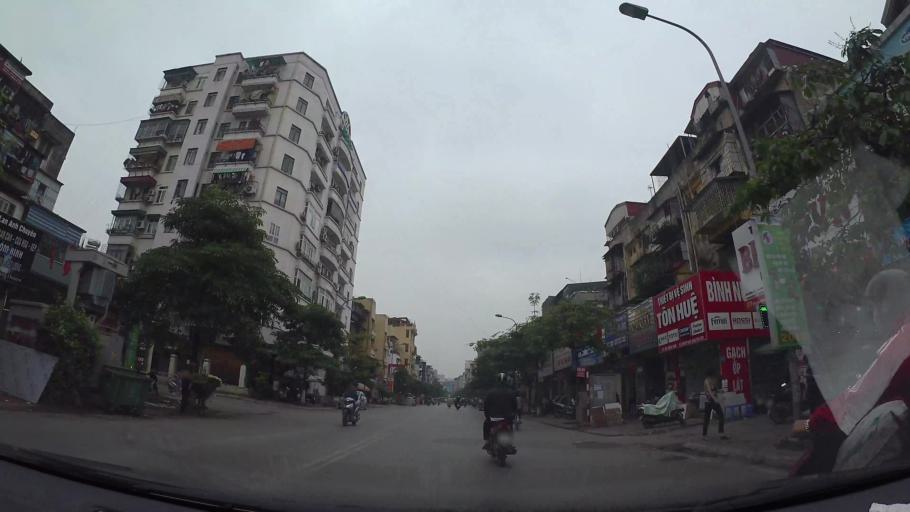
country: VN
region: Ha Noi
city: Hai BaTrung
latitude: 21.0029
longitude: 105.8526
